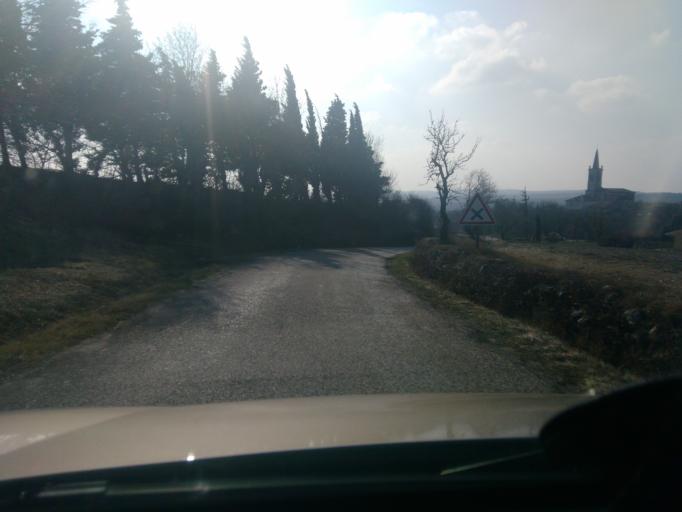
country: FR
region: Rhone-Alpes
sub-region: Departement de la Drome
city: Allan
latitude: 44.4769
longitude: 4.8559
